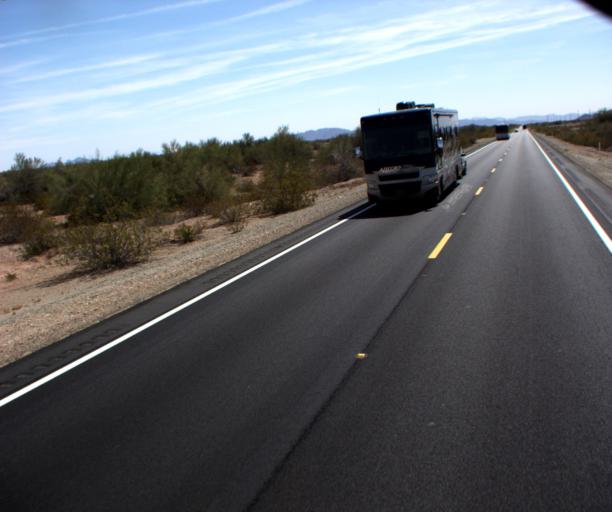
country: US
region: Arizona
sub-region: Yuma County
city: Wellton
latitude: 33.0010
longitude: -114.2859
